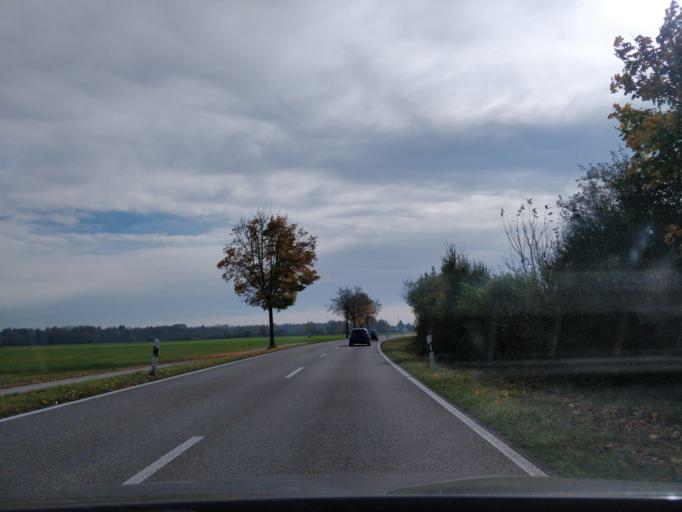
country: DE
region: Bavaria
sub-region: Swabia
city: Konigsbrunn
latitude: 48.2579
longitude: 10.9047
